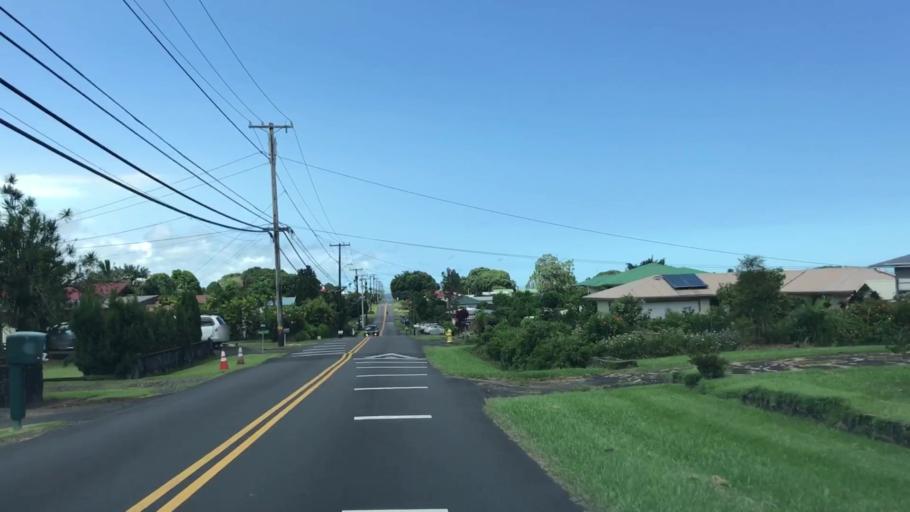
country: US
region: Hawaii
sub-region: Hawaii County
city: Hilo
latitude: 19.6751
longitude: -155.0798
